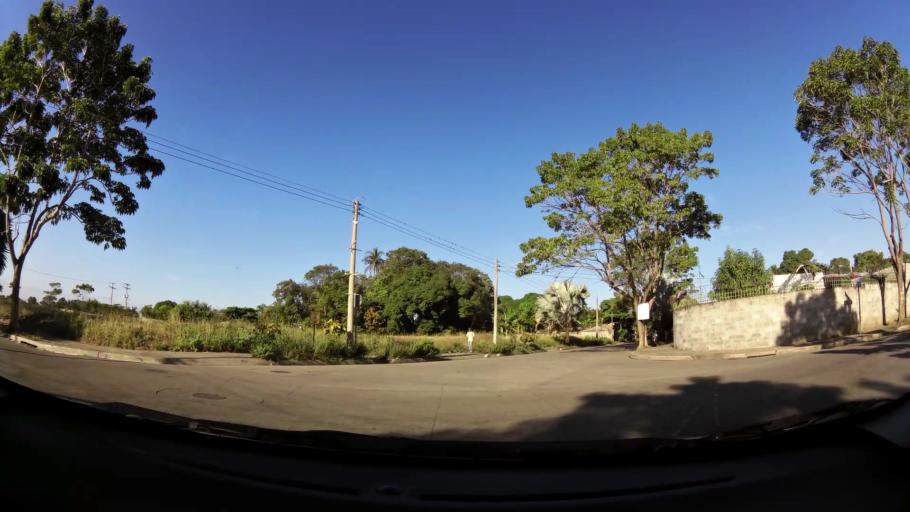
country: SV
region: Sonsonate
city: Sonsonate
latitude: 13.7121
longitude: -89.7197
